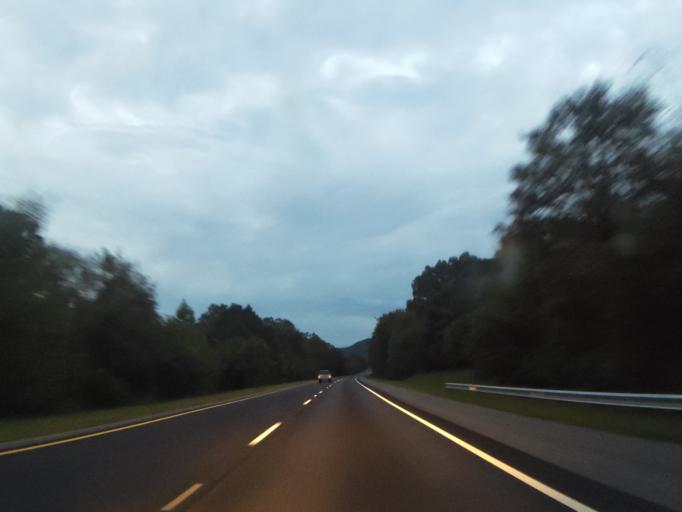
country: US
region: Alabama
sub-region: DeKalb County
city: Collinsville
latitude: 34.2132
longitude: -85.9318
